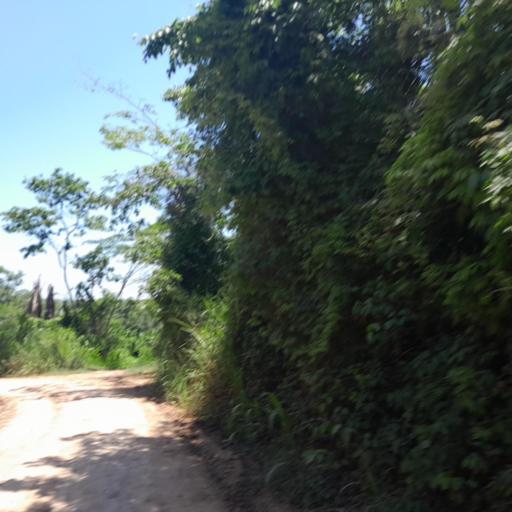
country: PE
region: Ucayali
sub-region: Provincia de Coronel Portillo
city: Puerto Callao
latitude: -8.2673
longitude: -74.6447
